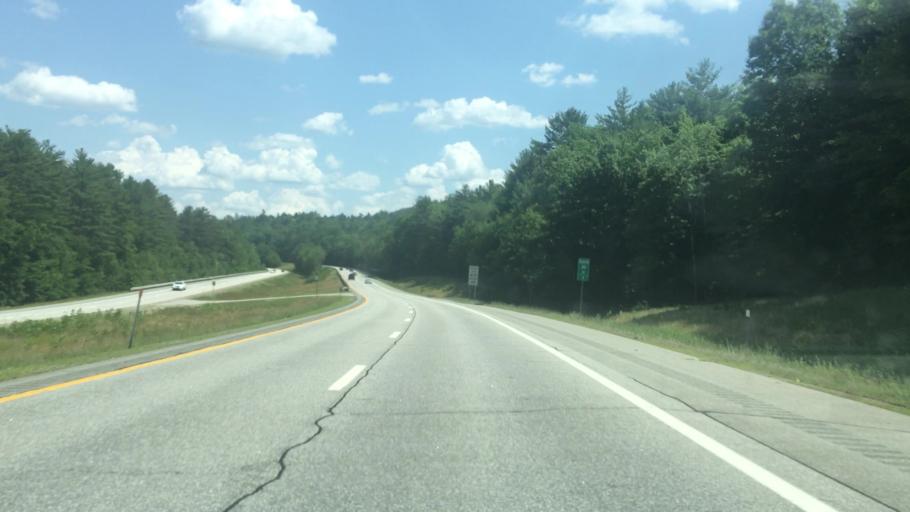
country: US
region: New Hampshire
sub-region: Merrimack County
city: Henniker
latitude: 43.2817
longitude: -71.8314
